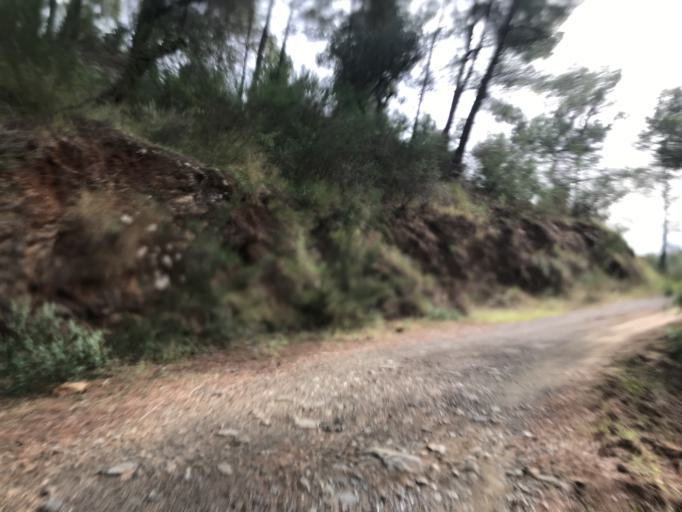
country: ES
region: Andalusia
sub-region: Provincia de Malaga
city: Malaga
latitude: 36.8029
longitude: -4.3993
